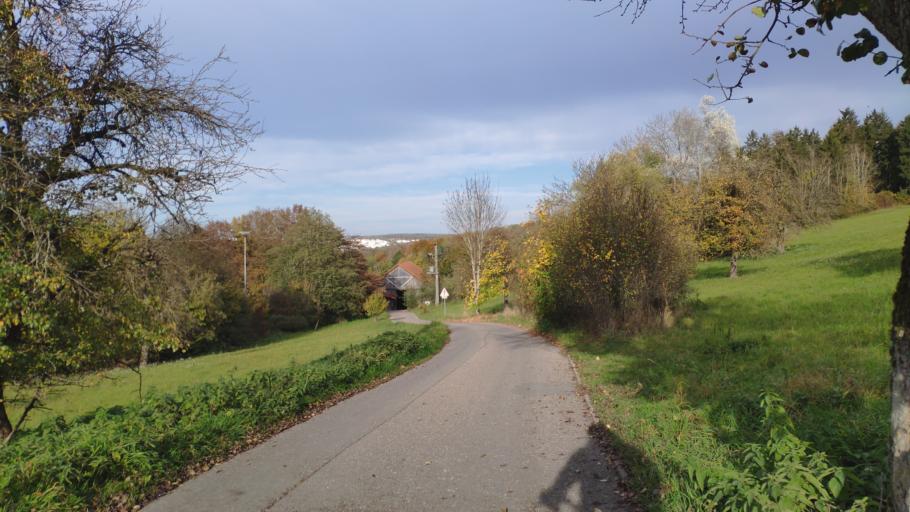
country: DE
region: Baden-Wuerttemberg
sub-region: Tuebingen Region
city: Erbach
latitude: 48.3807
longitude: 9.9192
